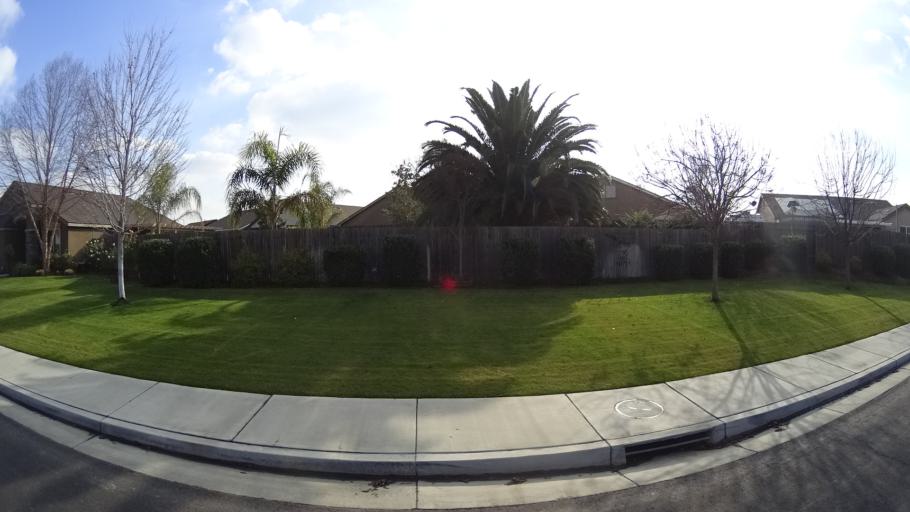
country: US
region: California
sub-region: Kern County
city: Greenacres
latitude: 35.3079
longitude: -119.1037
